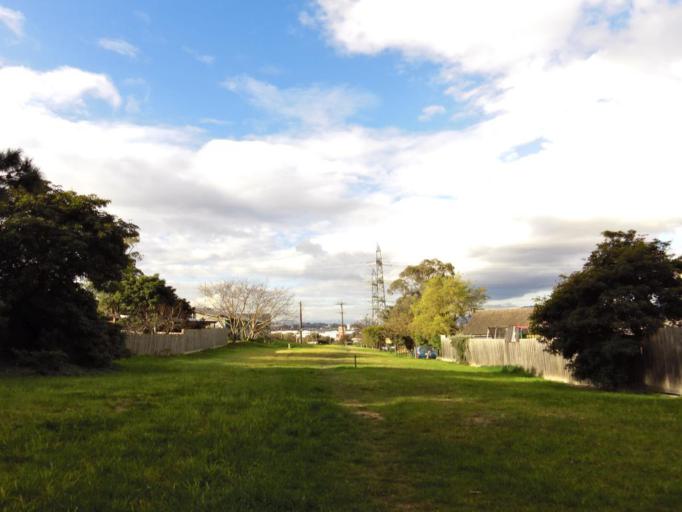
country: AU
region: Victoria
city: Mitcham
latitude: -37.8181
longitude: 145.2121
